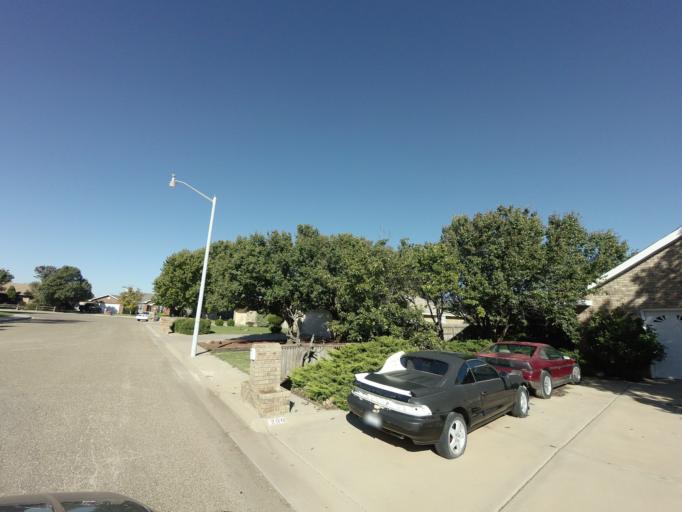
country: US
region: New Mexico
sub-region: Curry County
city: Clovis
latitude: 34.4316
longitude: -103.1762
